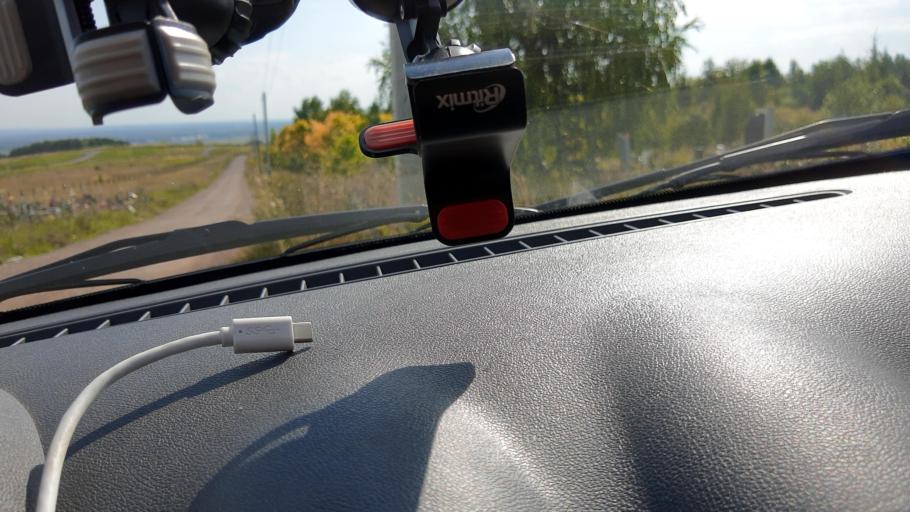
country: RU
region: Bashkortostan
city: Ufa
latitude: 54.8538
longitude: 56.1635
